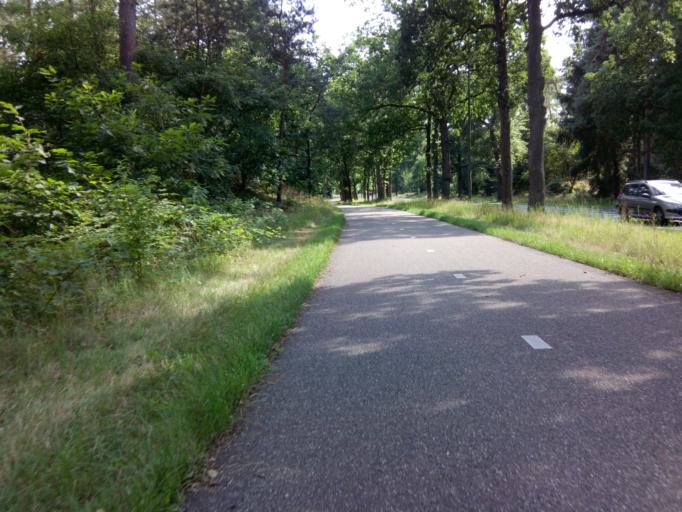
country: NL
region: Utrecht
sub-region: Gemeente Utrechtse Heuvelrug
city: Maarn
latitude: 52.0768
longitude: 5.3599
